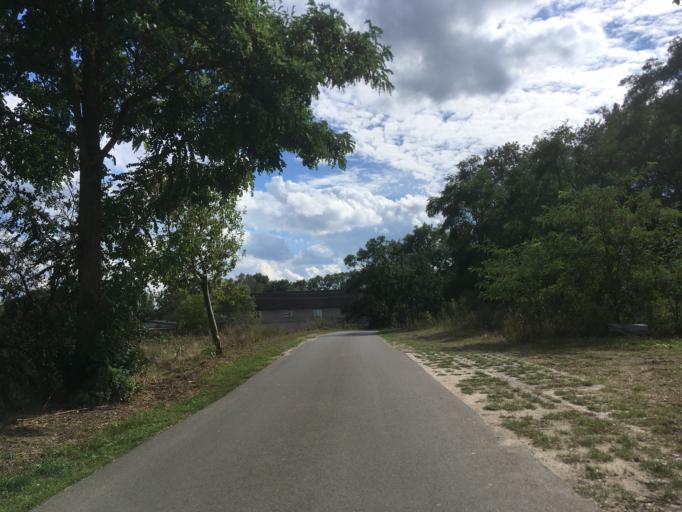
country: DE
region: Brandenburg
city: Angermunde
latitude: 52.9944
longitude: 14.0048
